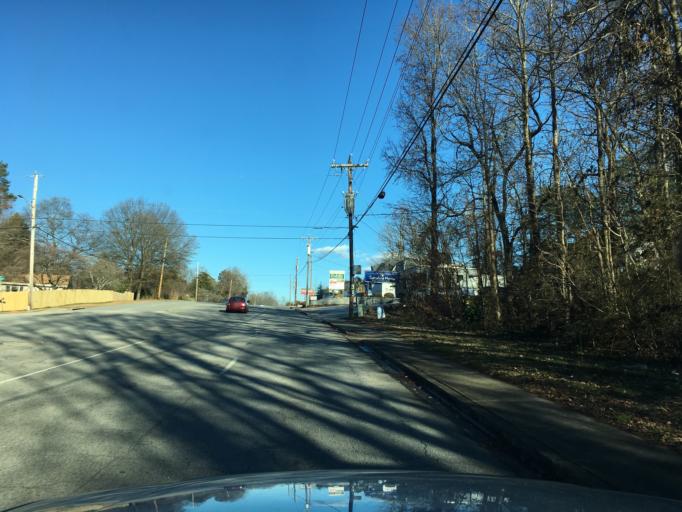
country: US
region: South Carolina
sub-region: Greenville County
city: Wade Hampton
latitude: 34.8697
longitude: -82.3504
